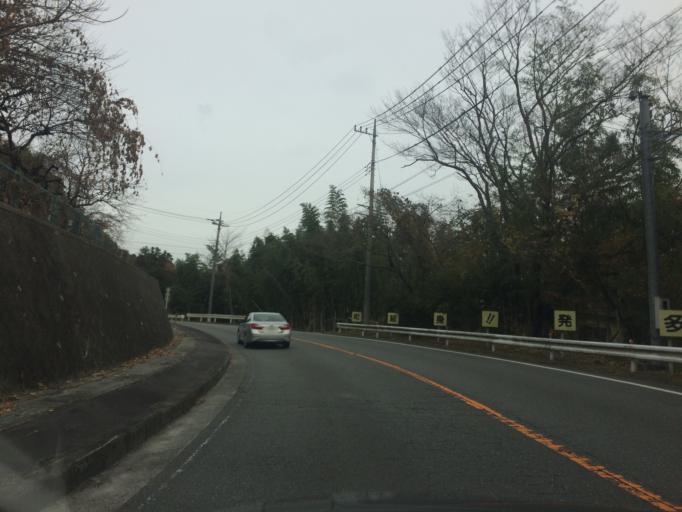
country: JP
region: Shizuoka
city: Fujinomiya
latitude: 35.3186
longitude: 138.4395
